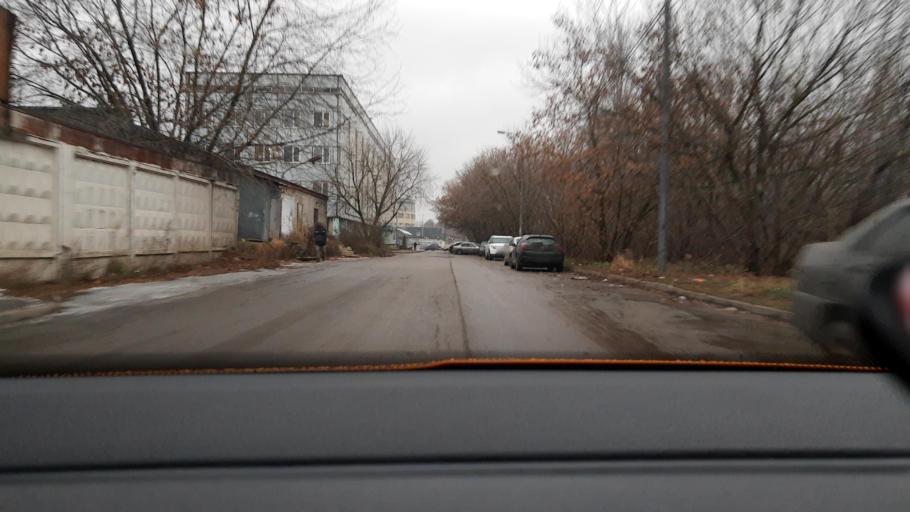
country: RU
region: Moscow
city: Strogino
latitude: 55.8287
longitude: 37.4043
